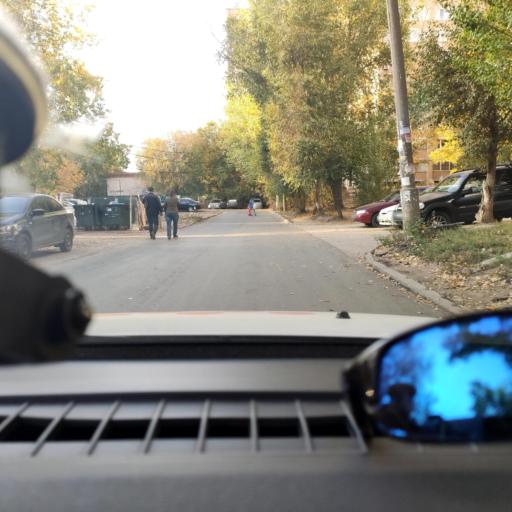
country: RU
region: Samara
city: Samara
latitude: 53.2482
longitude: 50.2242
